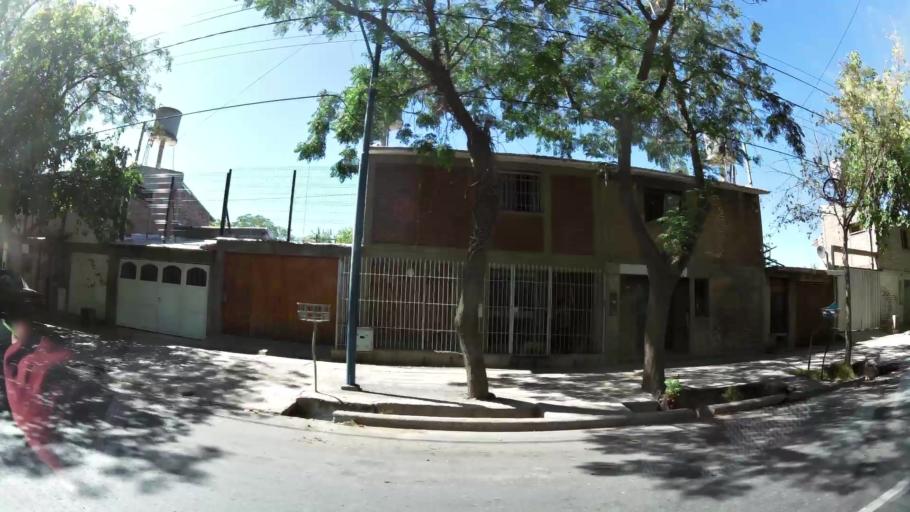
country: AR
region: Mendoza
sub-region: Departamento de Godoy Cruz
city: Godoy Cruz
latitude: -32.9563
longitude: -68.8409
